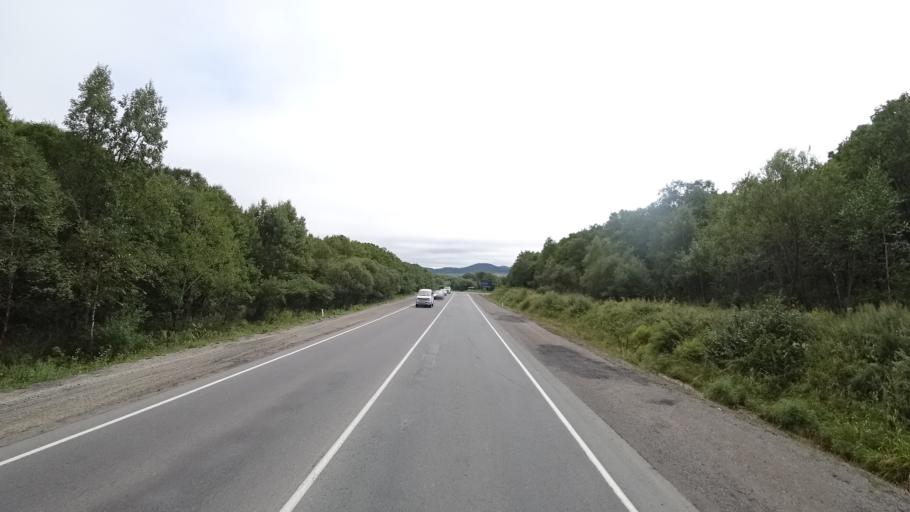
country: RU
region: Primorskiy
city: Lyalichi
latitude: 44.1019
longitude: 132.4240
